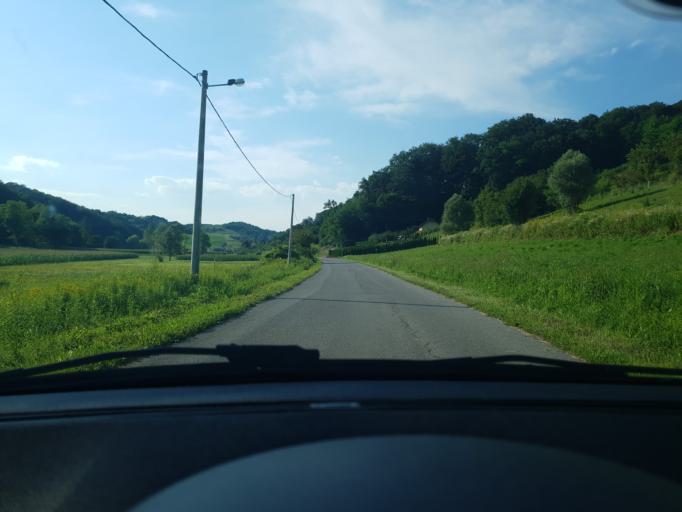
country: HR
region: Krapinsko-Zagorska
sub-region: Grad Krapina
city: Krapina
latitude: 46.1345
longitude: 15.8563
